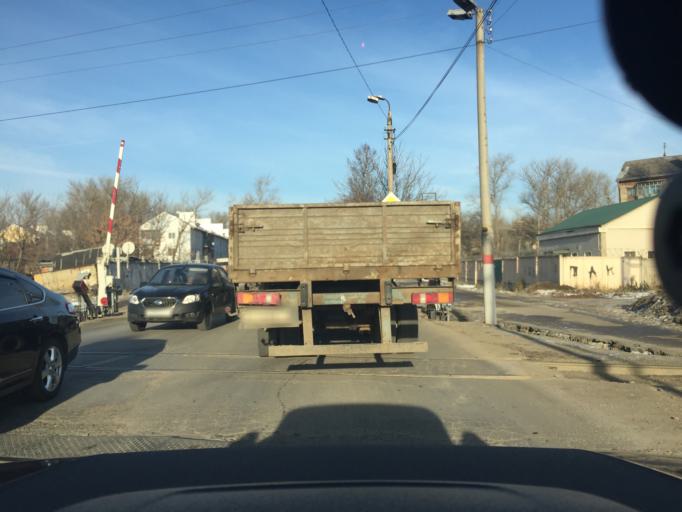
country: RU
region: Tula
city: Tula
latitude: 54.1772
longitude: 37.7051
